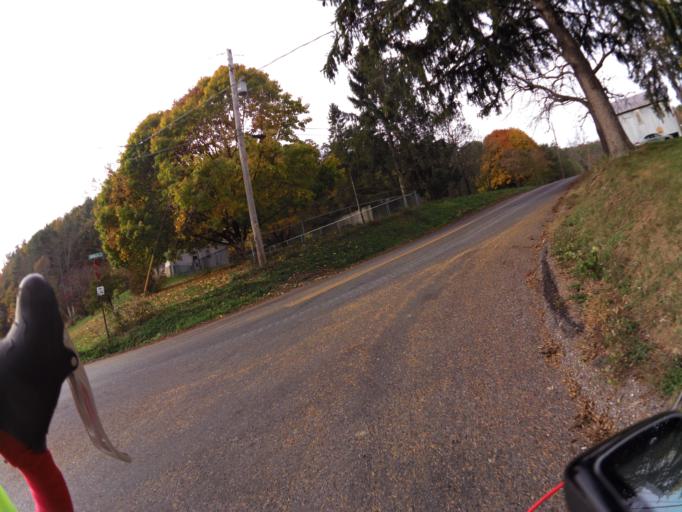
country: US
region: Pennsylvania
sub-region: Union County
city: New Columbia
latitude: 41.0338
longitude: -76.9446
